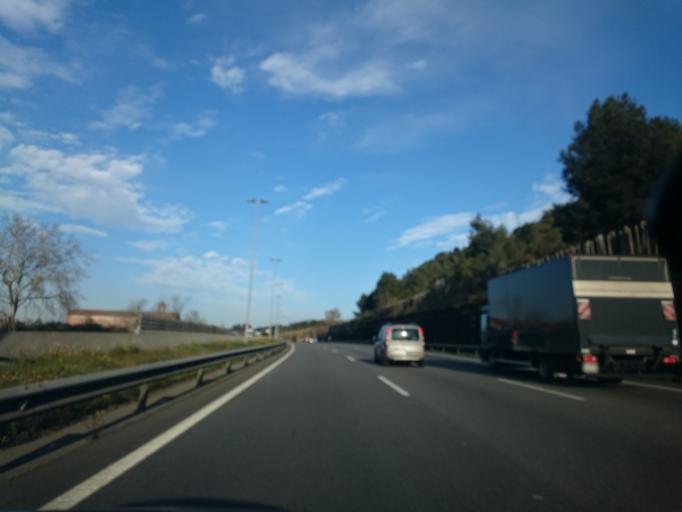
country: ES
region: Catalonia
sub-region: Provincia de Barcelona
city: Martorell
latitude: 41.4719
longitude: 1.9299
